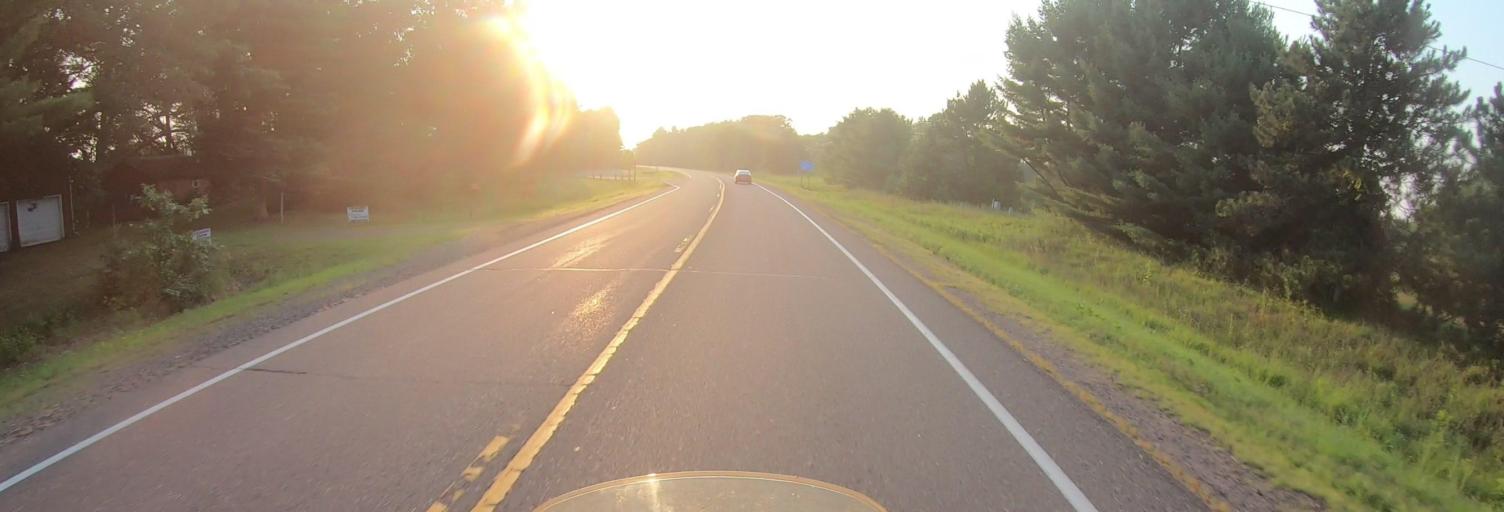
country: US
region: Wisconsin
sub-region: Burnett County
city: Siren
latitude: 45.8235
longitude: -92.2524
